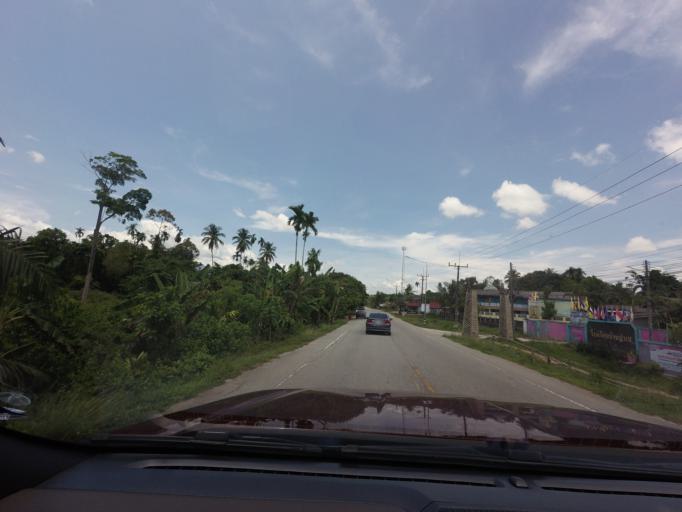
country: TH
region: Narathiwat
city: Chanae
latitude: 6.1945
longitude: 101.6882
